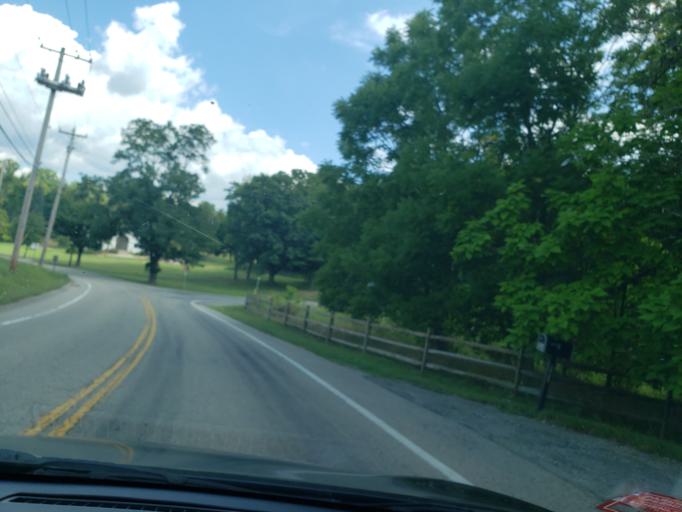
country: US
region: Pennsylvania
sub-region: Allegheny County
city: Coraopolis
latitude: 40.5455
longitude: -80.1480
